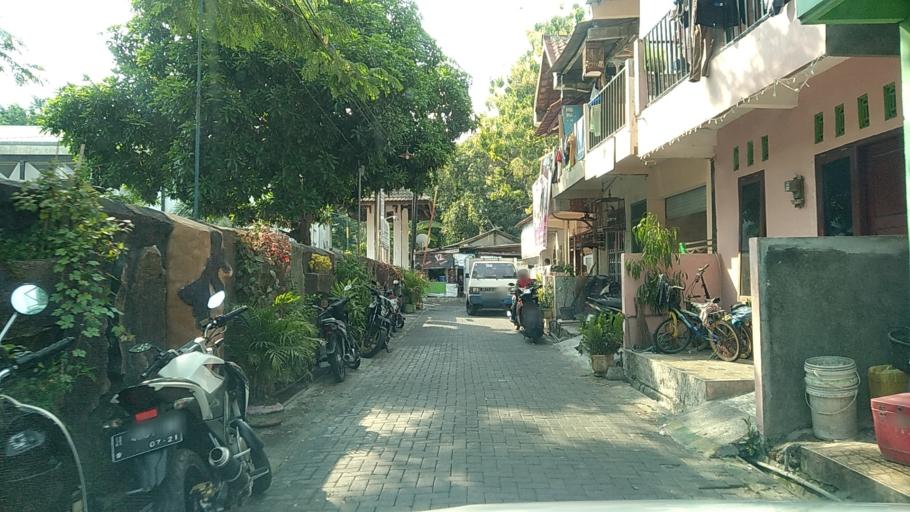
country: ID
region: Central Java
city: Semarang
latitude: -6.9973
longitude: 110.4228
